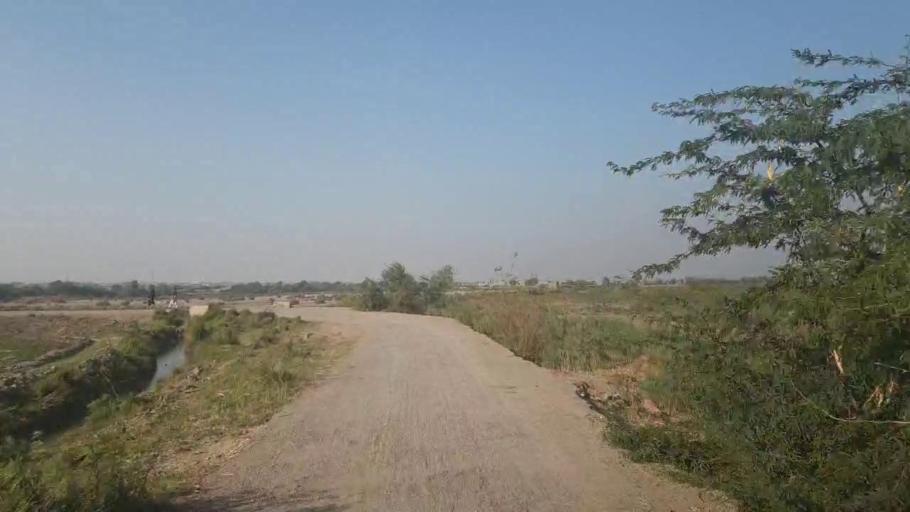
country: PK
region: Sindh
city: Kotri
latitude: 25.3935
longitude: 68.2902
